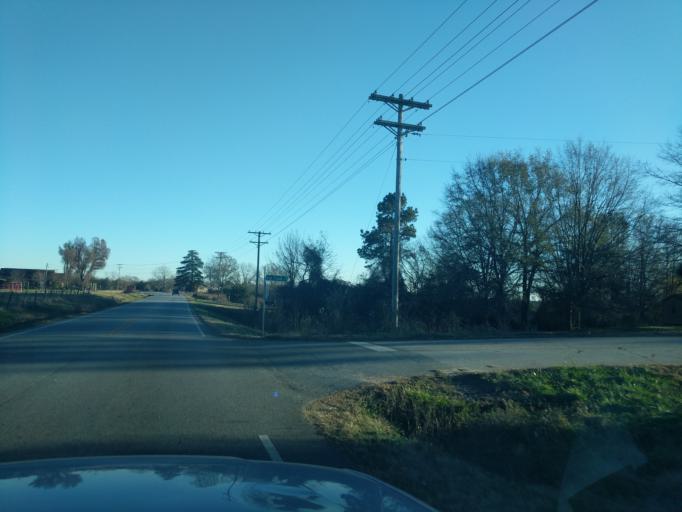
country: US
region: South Carolina
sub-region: Oconee County
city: Westminster
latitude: 34.6070
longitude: -83.0372
